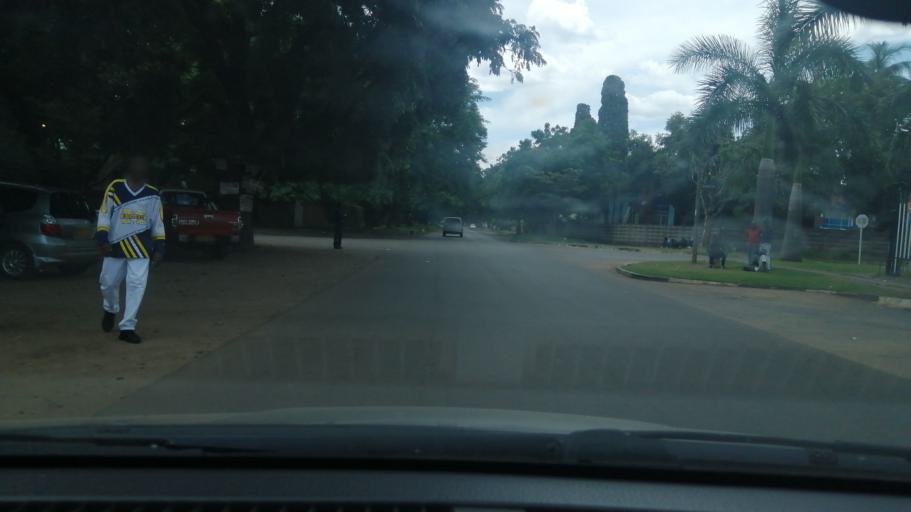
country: ZW
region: Harare
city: Harare
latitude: -17.8185
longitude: 31.0535
